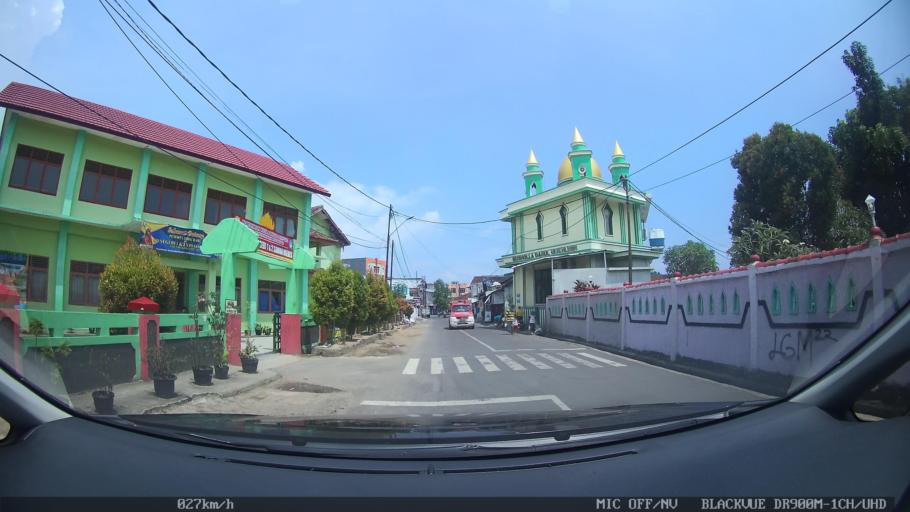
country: ID
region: Lampung
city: Bandarlampung
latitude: -5.4077
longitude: 105.2676
